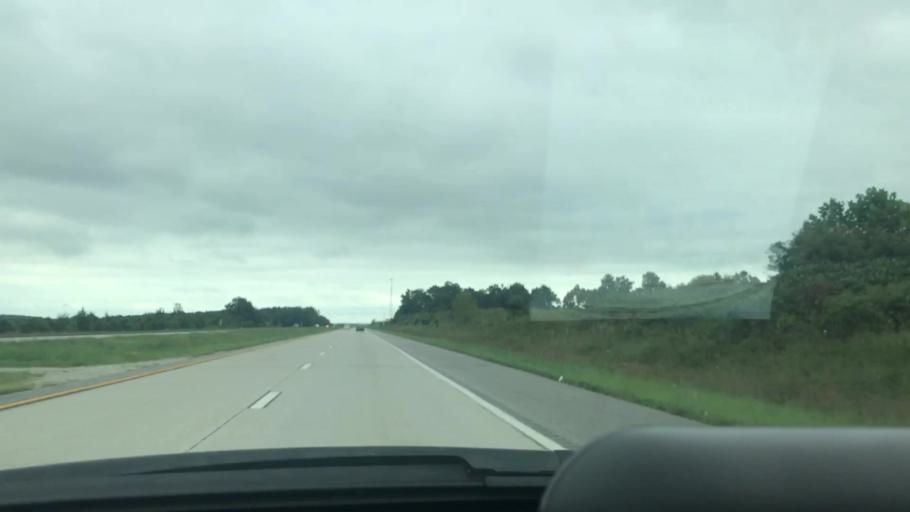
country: US
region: Missouri
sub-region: Greene County
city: Fair Grove
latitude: 37.4963
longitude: -93.1389
